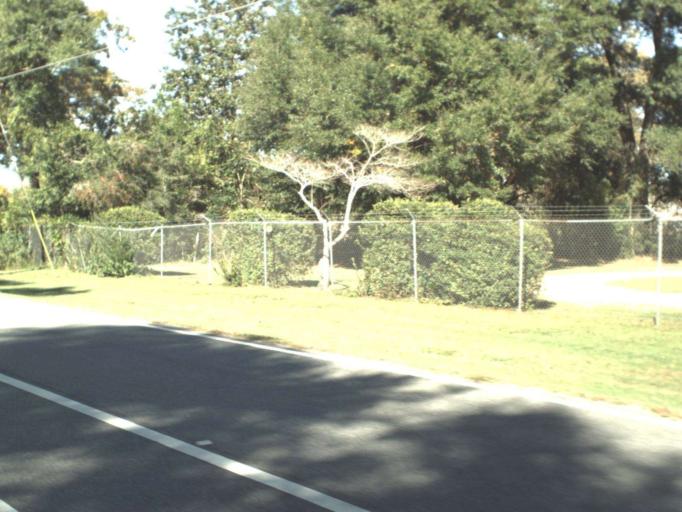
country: US
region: Florida
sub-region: Okaloosa County
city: Crestview
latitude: 30.7742
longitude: -86.6750
